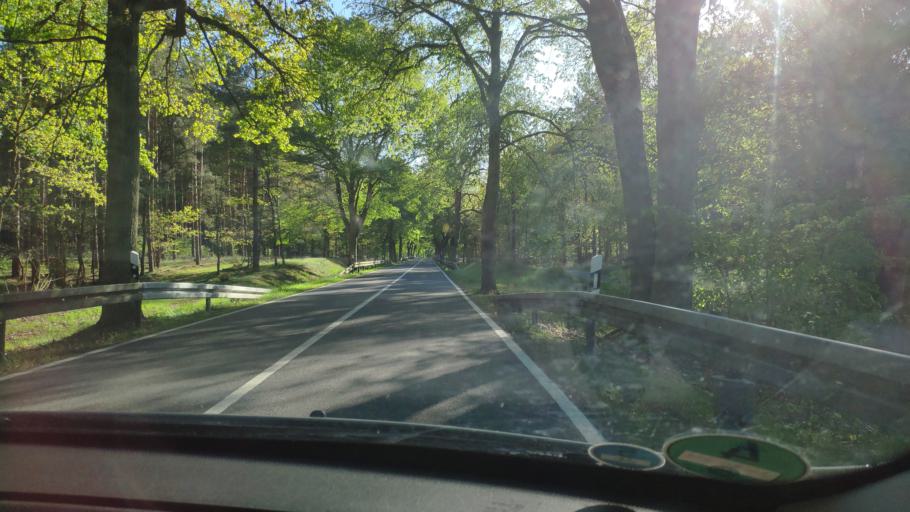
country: DE
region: Mecklenburg-Vorpommern
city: Wesenberg
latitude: 53.3297
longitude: 12.9162
